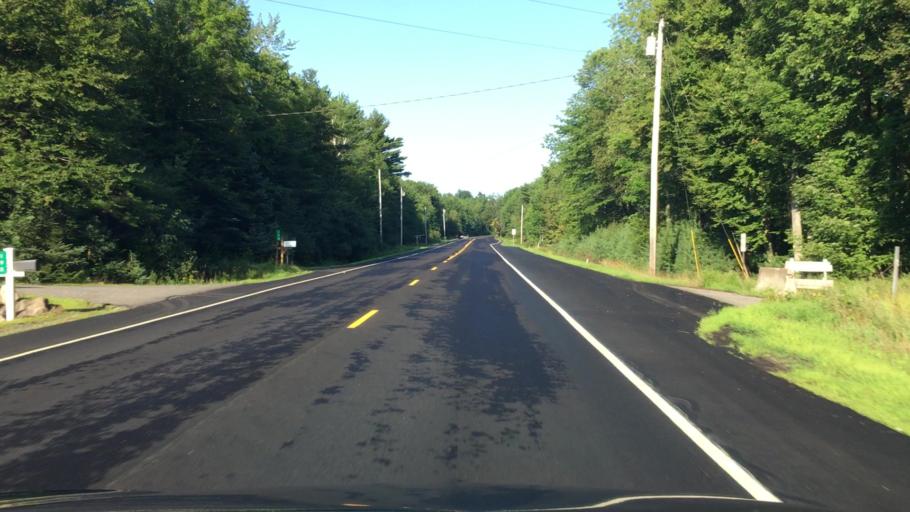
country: US
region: Maine
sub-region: Waldo County
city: Searsmont
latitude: 44.4017
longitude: -69.2398
